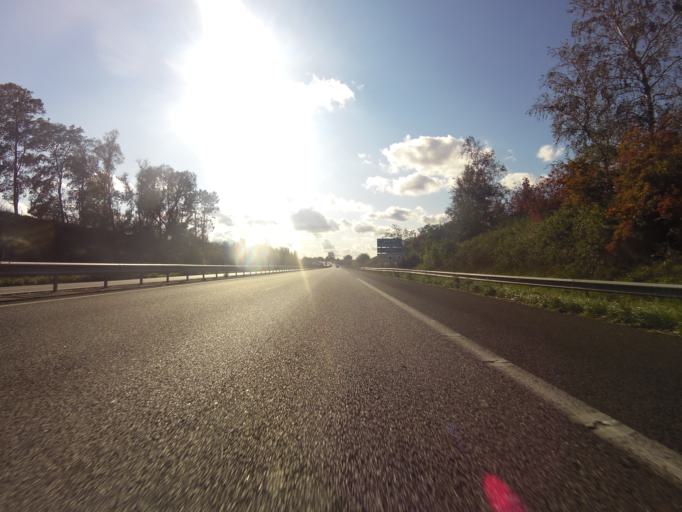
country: FR
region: Nord-Pas-de-Calais
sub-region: Departement du Pas-de-Calais
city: Bourlon
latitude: 50.1307
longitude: 3.1045
